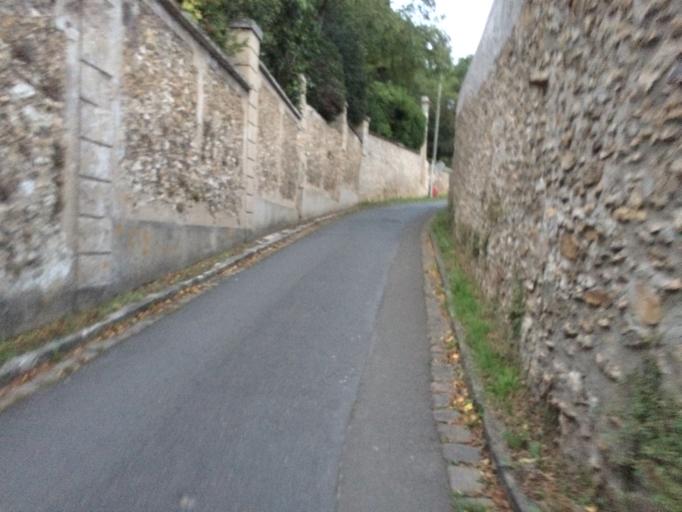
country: FR
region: Ile-de-France
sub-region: Departement des Yvelines
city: Velizy-Villacoublay
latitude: 48.7611
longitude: 2.1949
